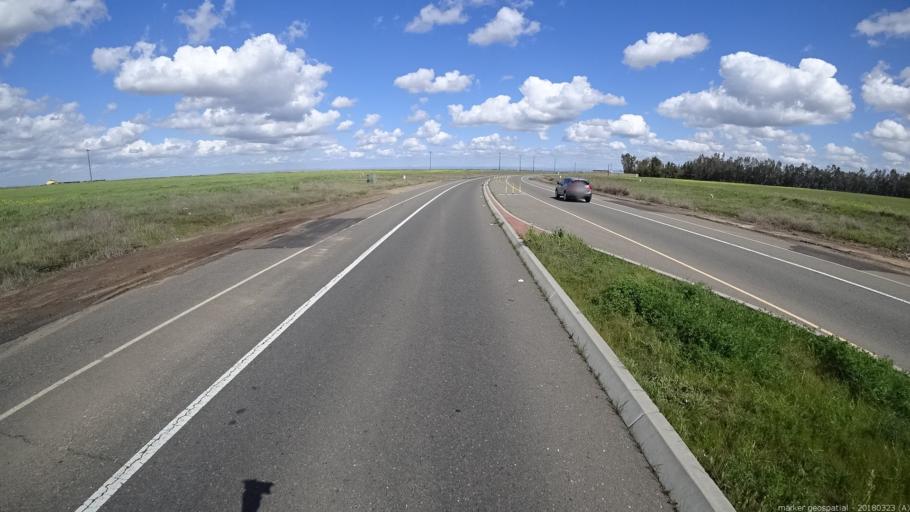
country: US
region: California
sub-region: Sacramento County
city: Elverta
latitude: 38.6839
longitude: -121.5651
